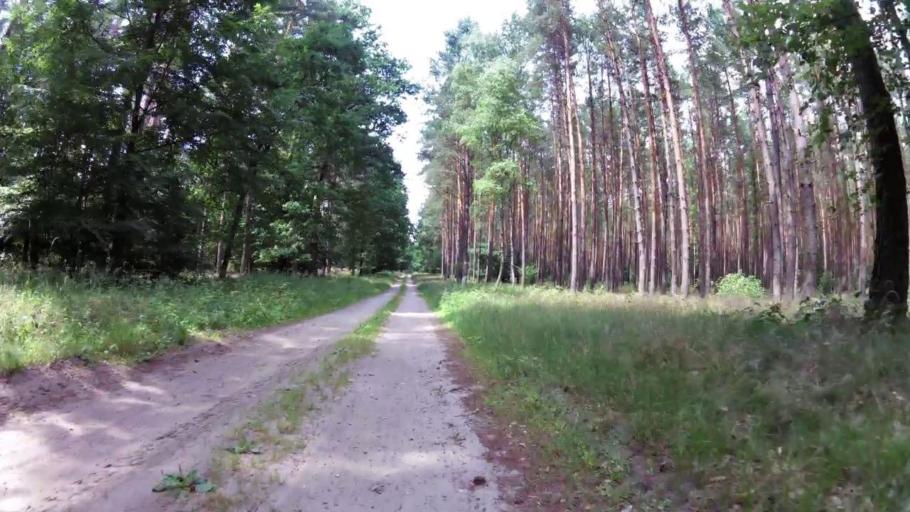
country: PL
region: West Pomeranian Voivodeship
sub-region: Powiat lobeski
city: Lobez
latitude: 53.5555
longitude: 15.6720
